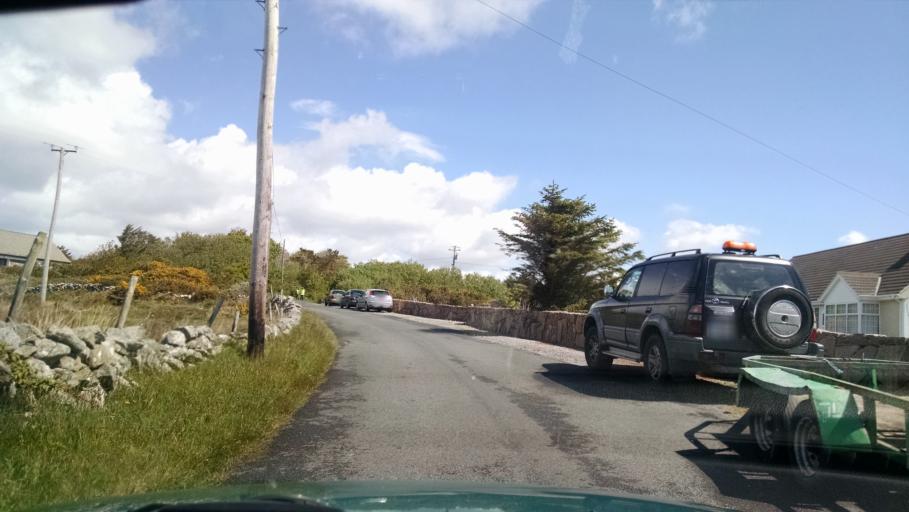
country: IE
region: Connaught
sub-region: County Galway
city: Oughterard
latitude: 53.2492
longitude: -9.6199
